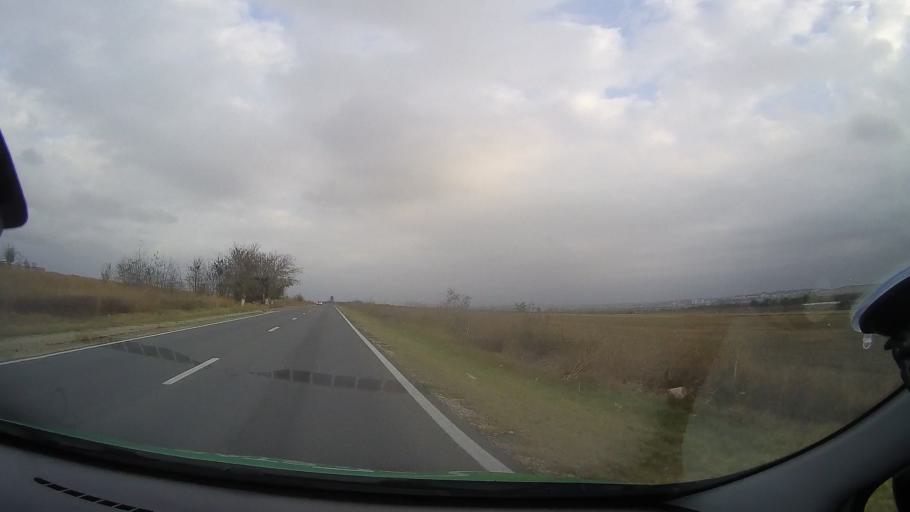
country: RO
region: Constanta
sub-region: Comuna Mircea Voda
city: Satu Nou
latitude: 44.2655
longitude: 28.2378
